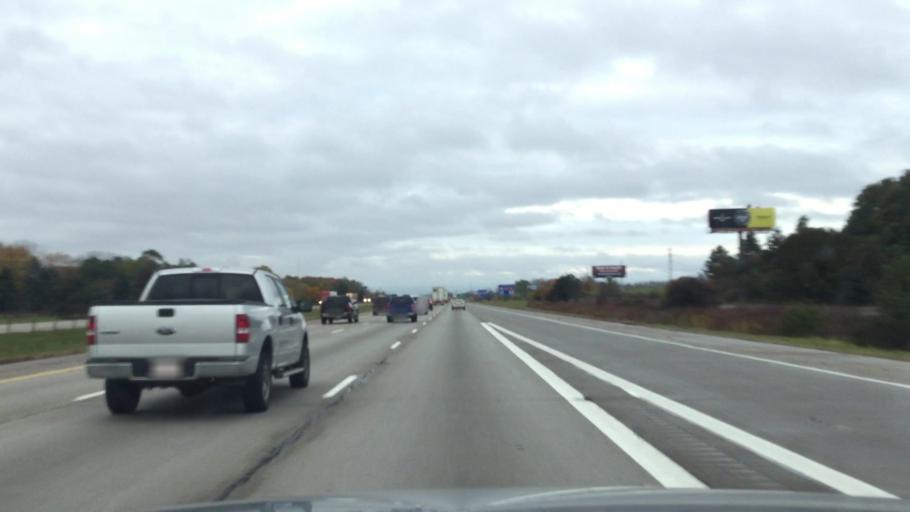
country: US
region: Michigan
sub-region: Wayne County
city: Belleville
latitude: 42.2188
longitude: -83.5250
